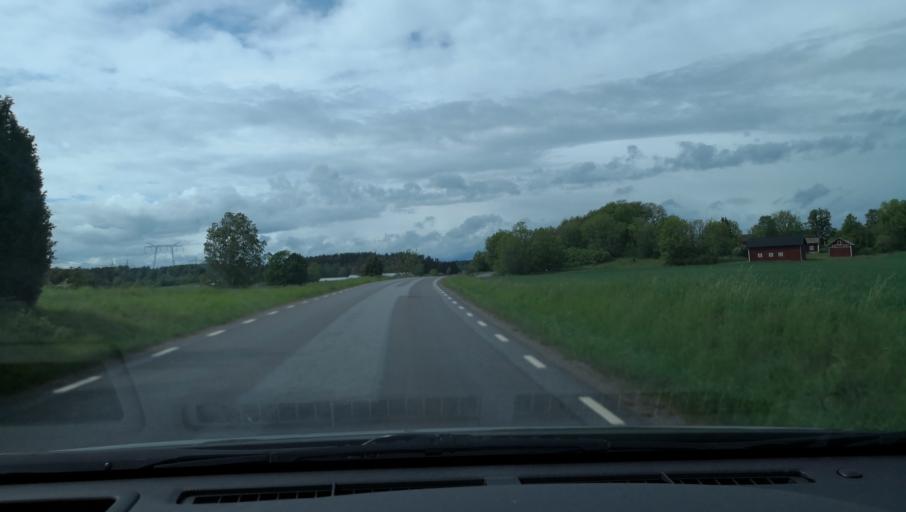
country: SE
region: Uppsala
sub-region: Enkopings Kommun
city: Orsundsbro
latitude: 59.6993
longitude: 17.3655
